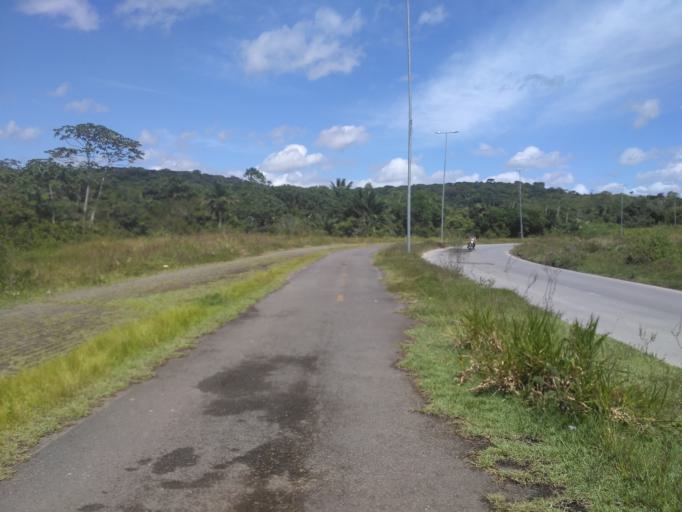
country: BR
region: Pernambuco
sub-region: Sao Lourenco Da Mata
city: Sao Lourenco da Mata
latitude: -8.0435
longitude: -34.9979
